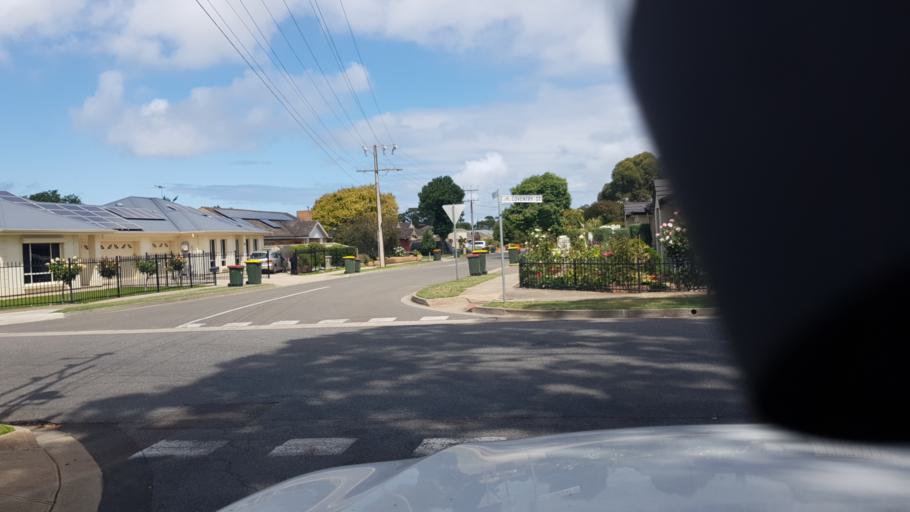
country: AU
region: South Australia
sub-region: Adelaide
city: Brighton
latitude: -35.0170
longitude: 138.5315
